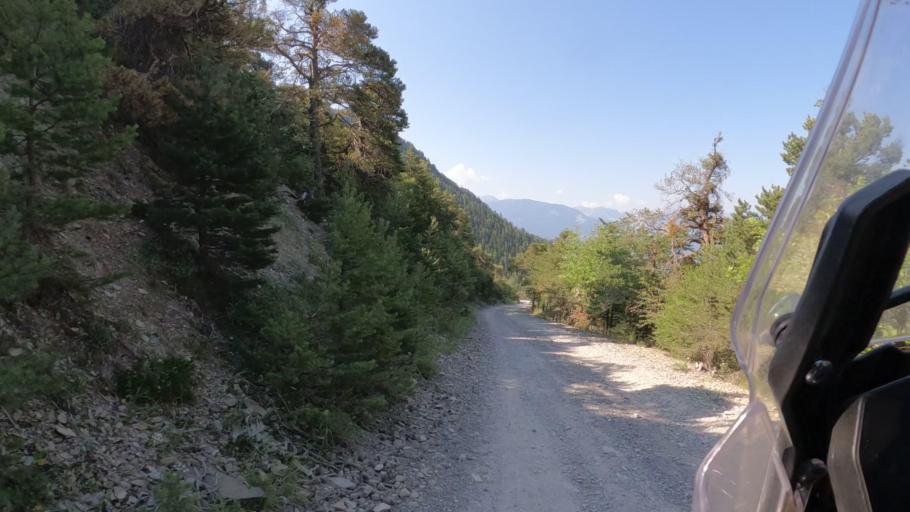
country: FR
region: Provence-Alpes-Cote d'Azur
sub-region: Departement des Hautes-Alpes
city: Embrun
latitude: 44.5865
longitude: 6.5526
